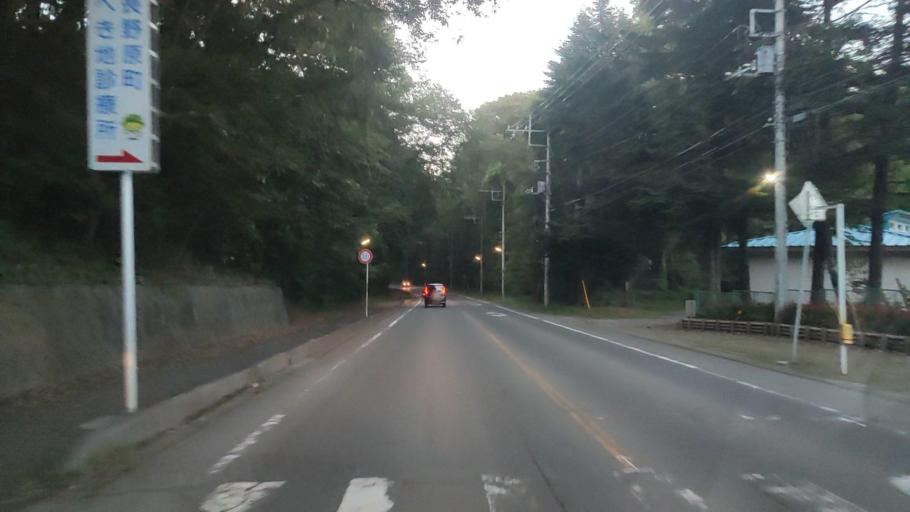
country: JP
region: Nagano
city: Komoro
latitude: 36.5032
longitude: 138.5905
